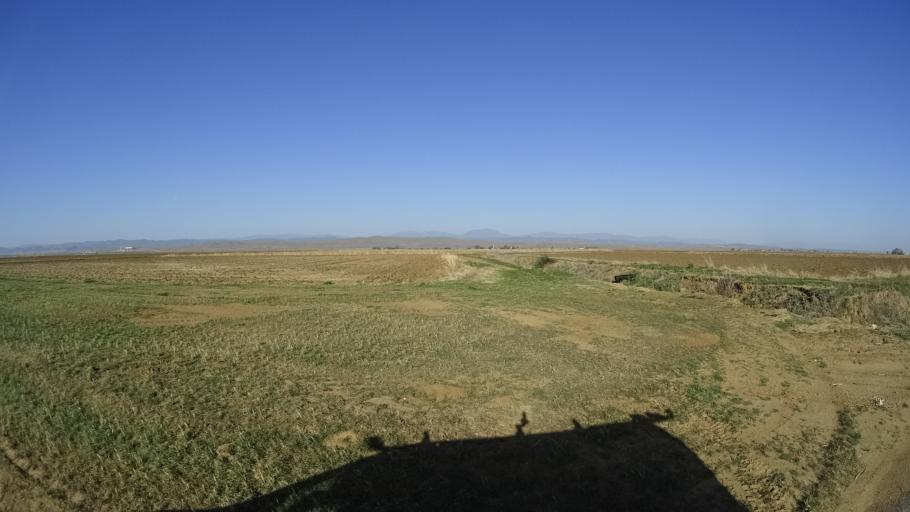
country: US
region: California
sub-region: Colusa County
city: Maxwell
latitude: 39.3938
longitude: -122.2301
